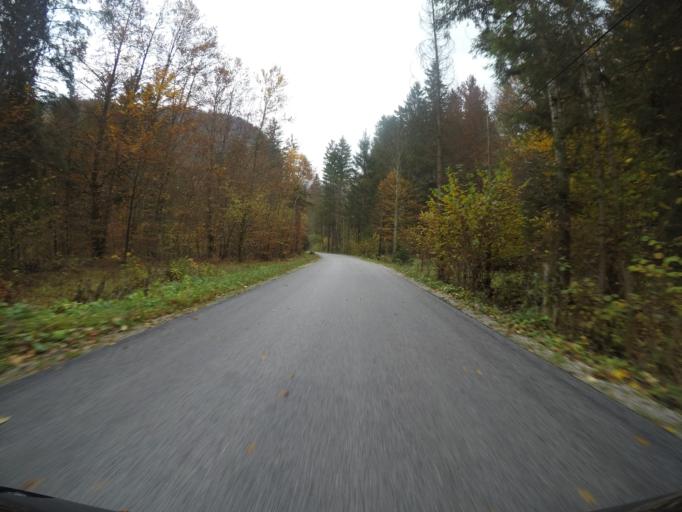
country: SI
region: Jesenice
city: Hrusica
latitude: 46.4140
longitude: 13.9923
